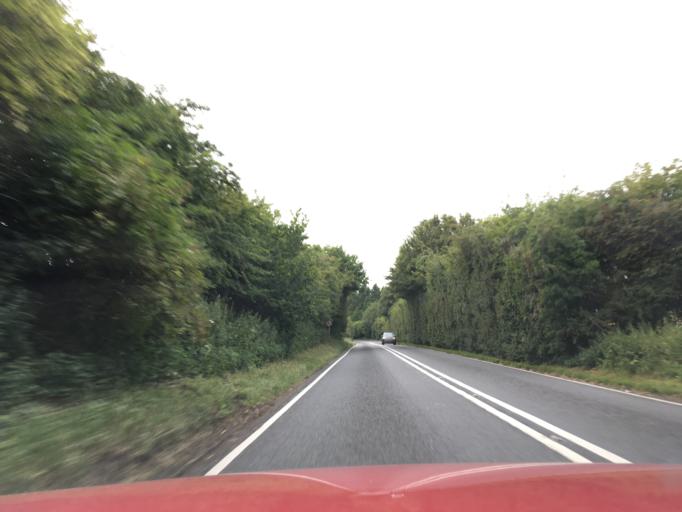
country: GB
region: England
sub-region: Hampshire
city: Petersfield
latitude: 51.0165
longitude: -1.0094
